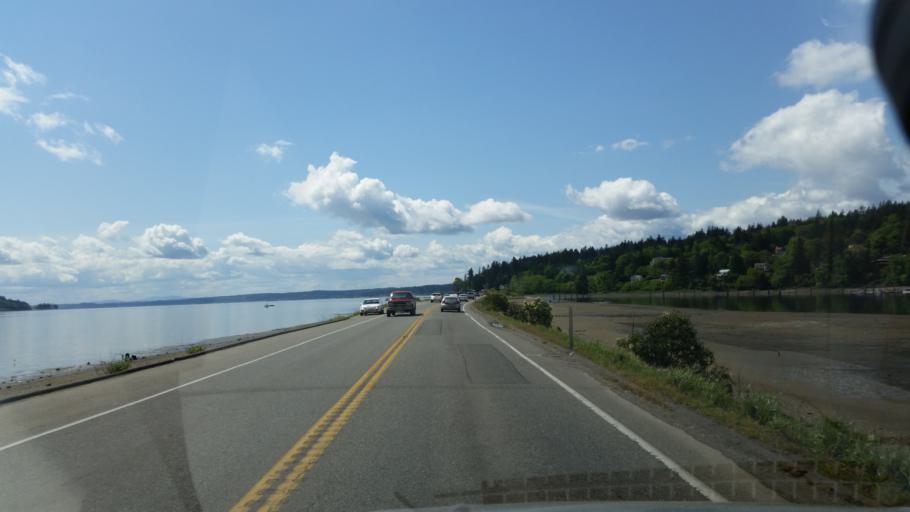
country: US
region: Washington
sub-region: Pierce County
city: Purdy
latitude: 47.3834
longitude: -122.6299
